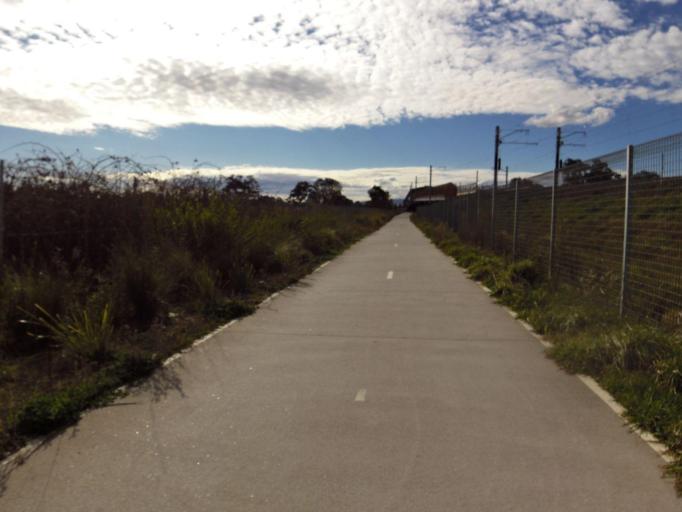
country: AU
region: Victoria
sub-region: Whittlesea
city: Mernda
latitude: -37.6058
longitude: 145.1000
